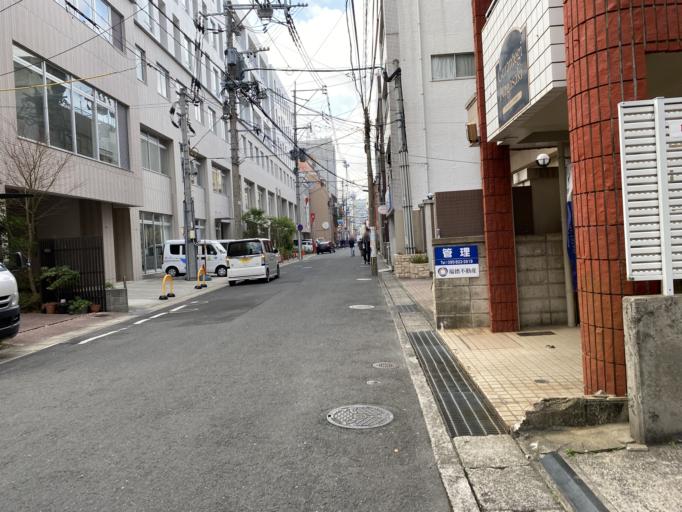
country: JP
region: Nagasaki
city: Nagasaki-shi
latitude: 32.7456
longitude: 129.8813
